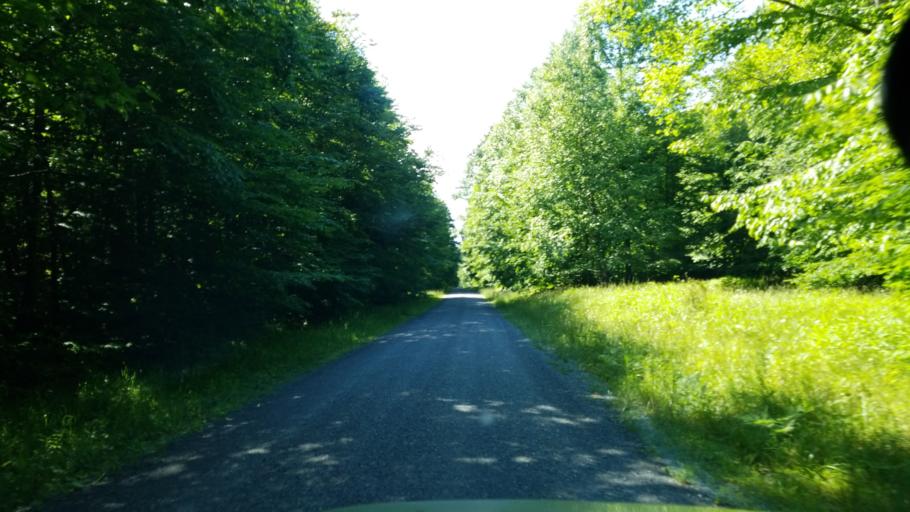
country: US
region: Pennsylvania
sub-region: Clearfield County
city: Clearfield
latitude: 41.2046
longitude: -78.4878
